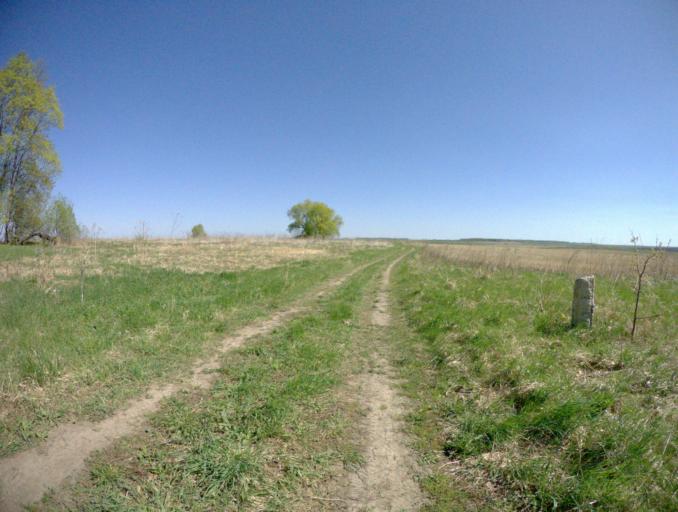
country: RU
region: Vladimir
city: Vladimir
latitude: 56.2817
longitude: 40.3181
